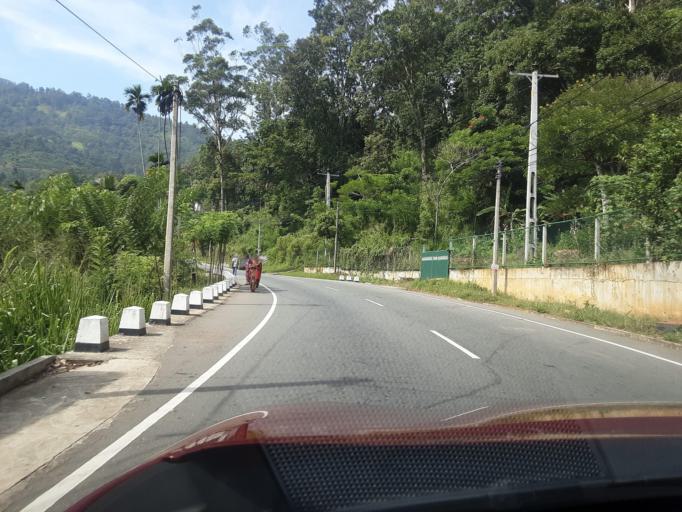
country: LK
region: Uva
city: Badulla
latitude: 6.9703
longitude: 81.0862
